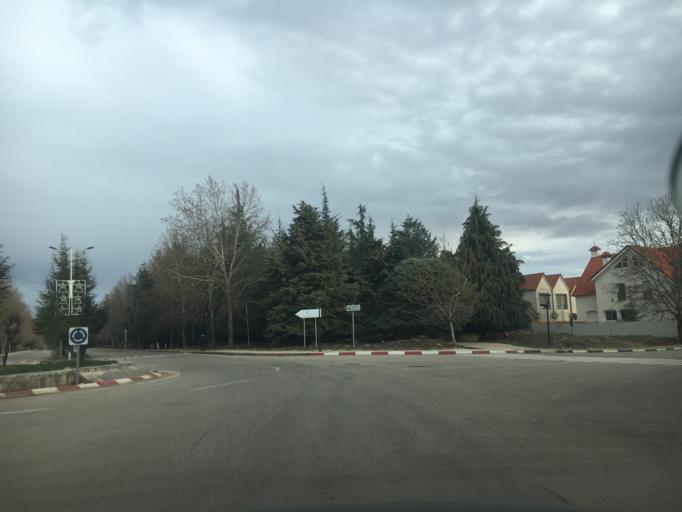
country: MA
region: Meknes-Tafilalet
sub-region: Ifrane
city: Ifrane
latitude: 33.5286
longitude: -5.1300
